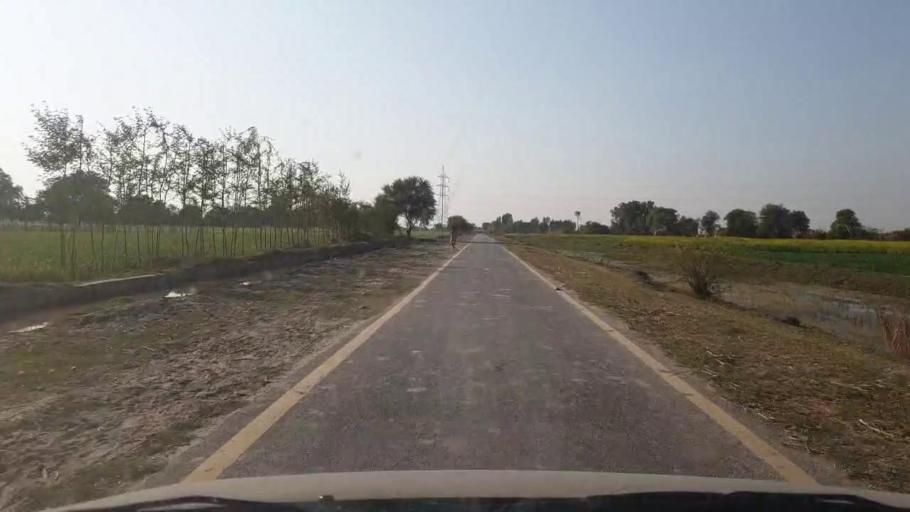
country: PK
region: Sindh
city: Samaro
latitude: 25.2866
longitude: 69.3585
